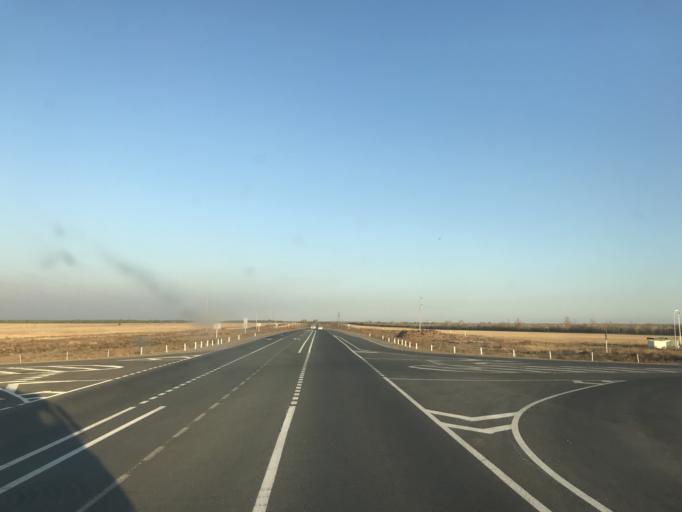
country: KZ
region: Pavlodar
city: Kurchatov
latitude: 50.9610
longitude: 79.3370
